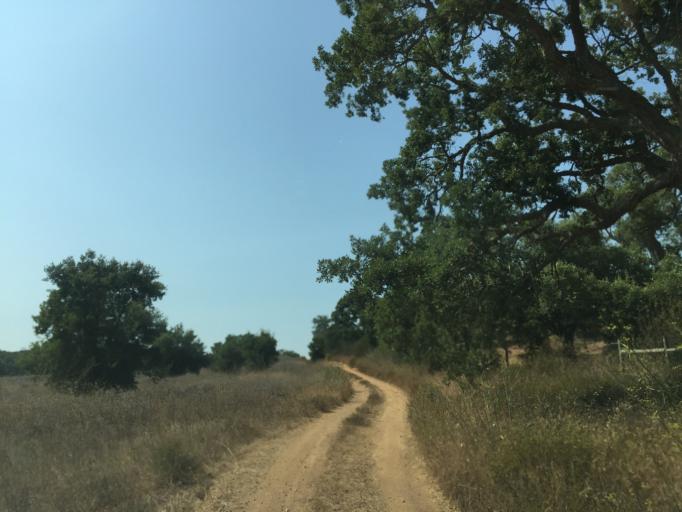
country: PT
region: Setubal
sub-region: Santiago do Cacem
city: Santiago do Cacem
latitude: 37.9717
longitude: -8.5136
